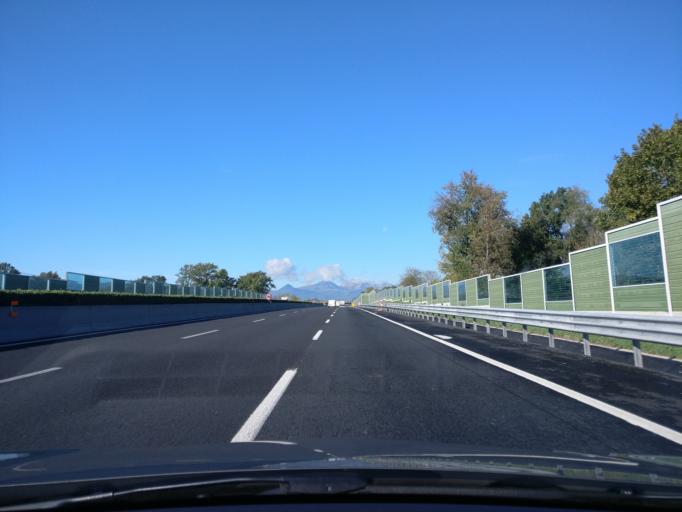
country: IT
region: Latium
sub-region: Provincia di Frosinone
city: Pofi
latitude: 41.5535
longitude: 13.4382
